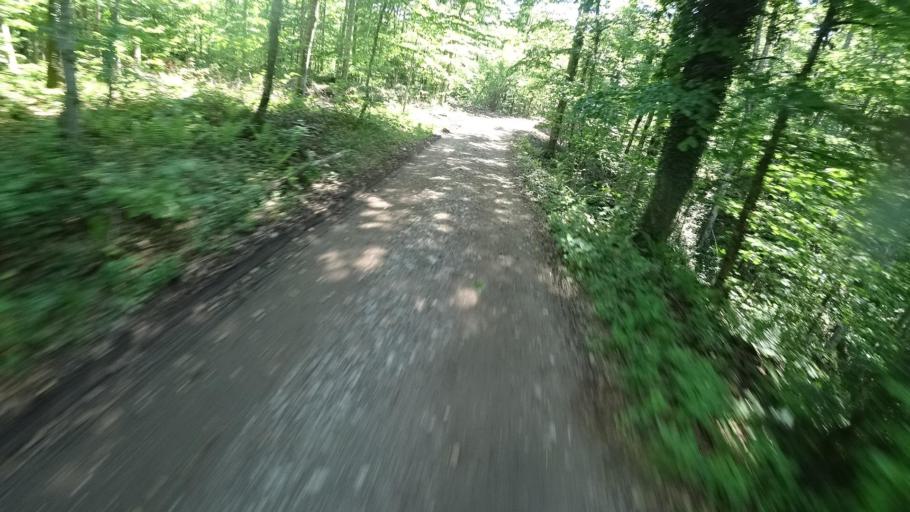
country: BA
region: Federation of Bosnia and Herzegovina
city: Bosanska Krupa
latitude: 44.7507
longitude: 16.2789
